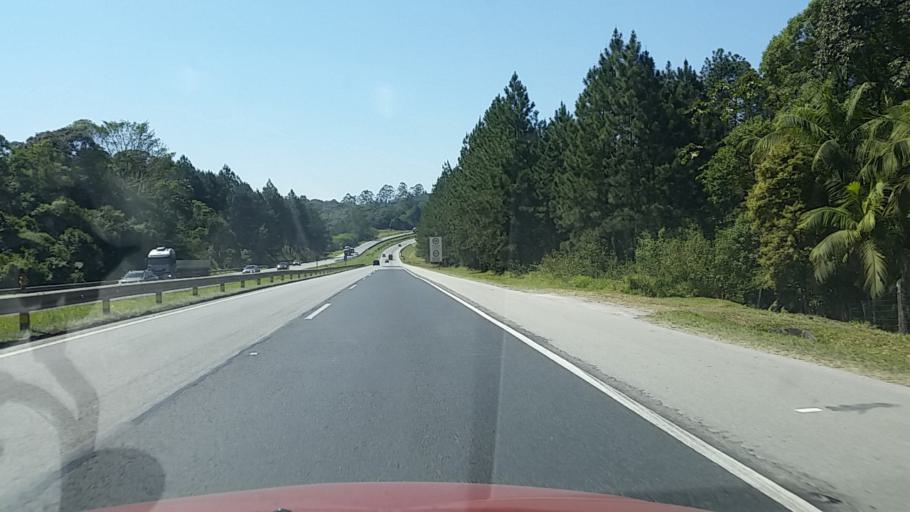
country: BR
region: Sao Paulo
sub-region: Juquitiba
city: Juquitiba
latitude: -23.9716
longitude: -47.1352
